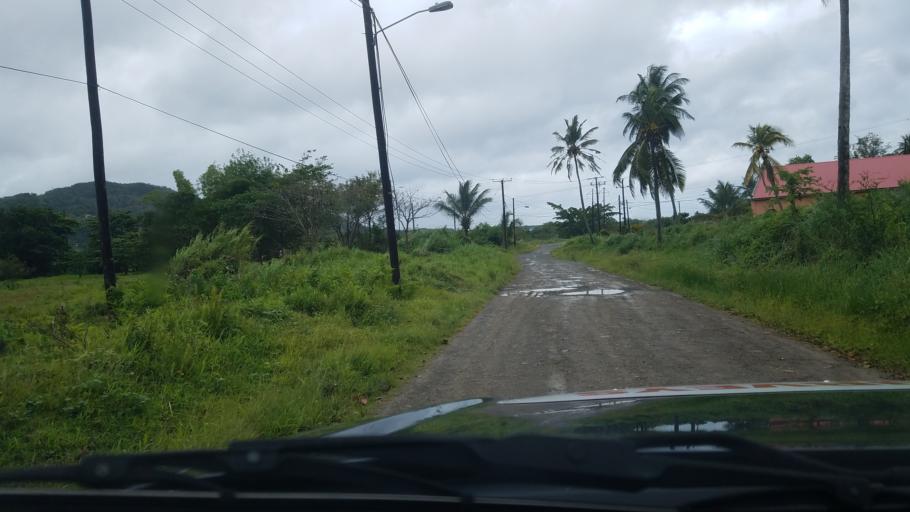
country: LC
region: Castries Quarter
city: Castries
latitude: 13.9860
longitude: -60.9963
